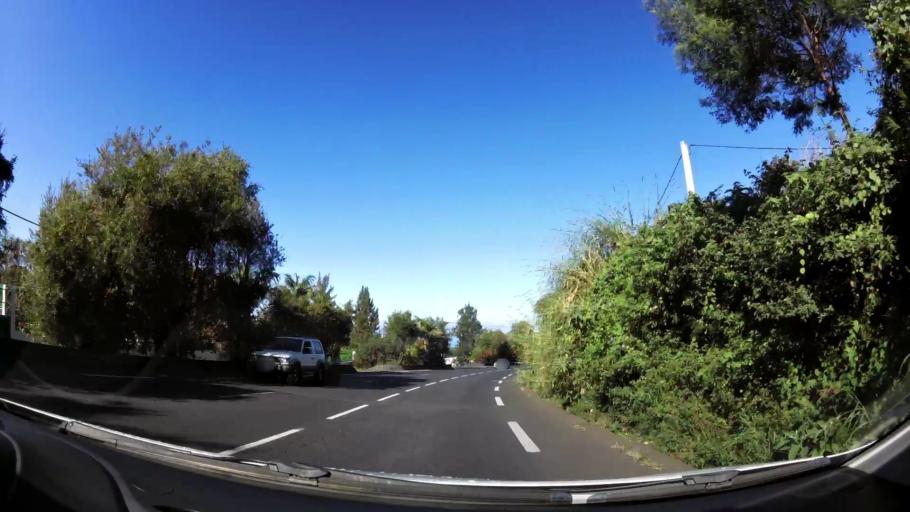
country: RE
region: Reunion
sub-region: Reunion
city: Le Tampon
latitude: -21.2390
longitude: 55.5299
